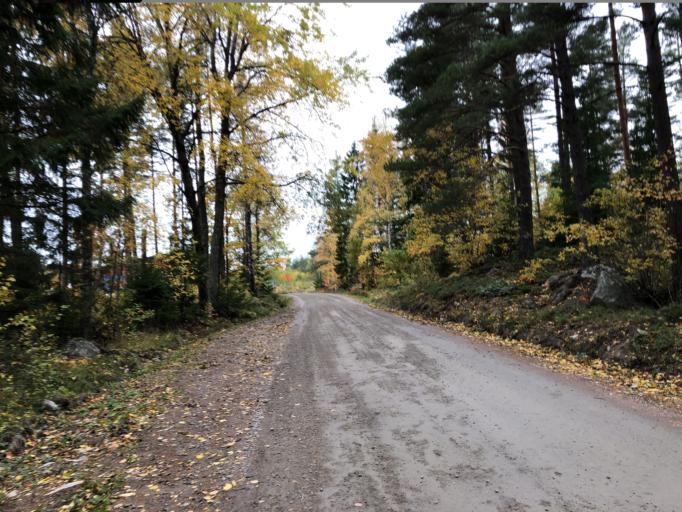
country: SE
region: Soedermanland
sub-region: Nykopings Kommun
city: Nykoping
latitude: 58.7172
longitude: 17.0354
